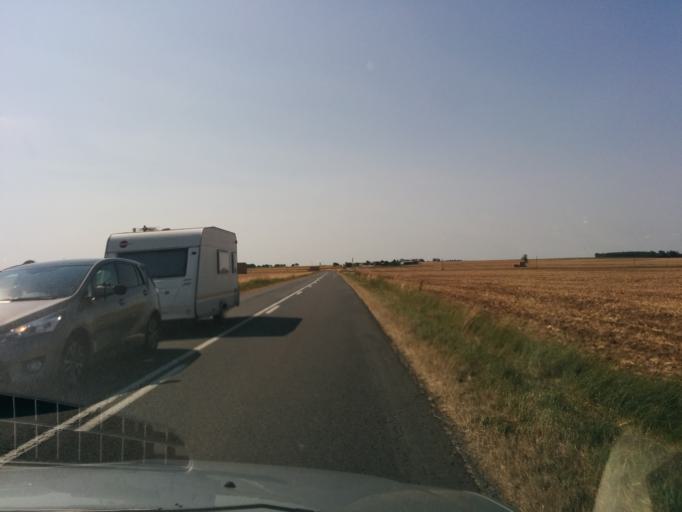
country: FR
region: Poitou-Charentes
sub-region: Departement de la Vienne
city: Mirebeau
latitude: 46.7880
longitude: 0.1228
